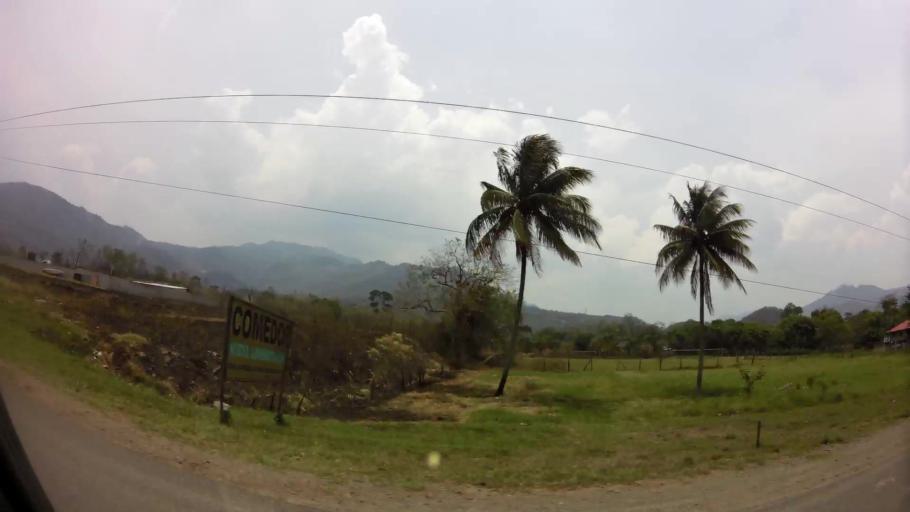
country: HN
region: Comayagua
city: Taulabe
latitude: 14.7095
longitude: -87.9630
